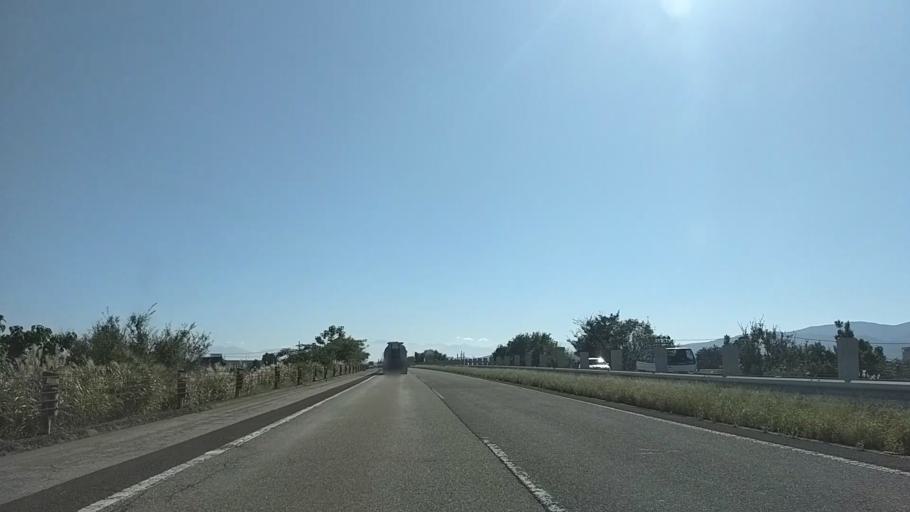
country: JP
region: Toyama
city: Nanto-shi
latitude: 36.6232
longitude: 136.9396
